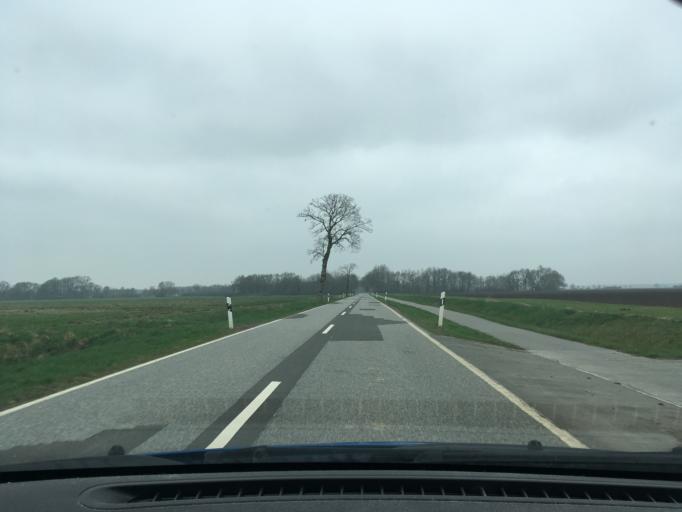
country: DE
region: Lower Saxony
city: Neu Darchau
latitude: 53.3179
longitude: 10.8371
